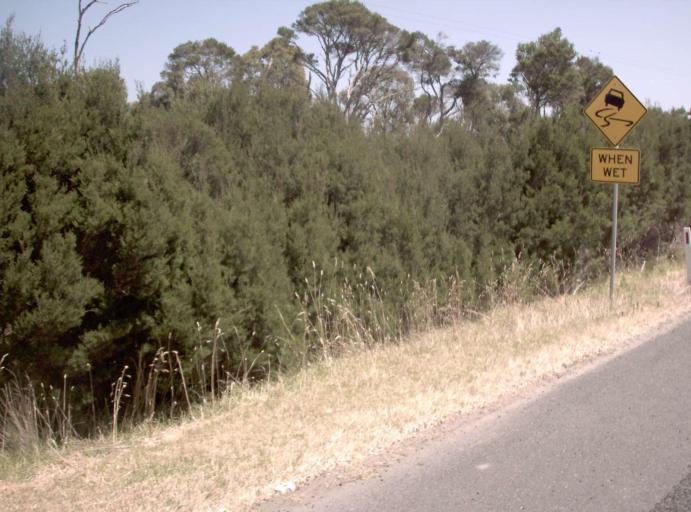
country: AU
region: Victoria
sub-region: Cardinia
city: Koo-Wee-Rup
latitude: -38.2123
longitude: 145.4443
